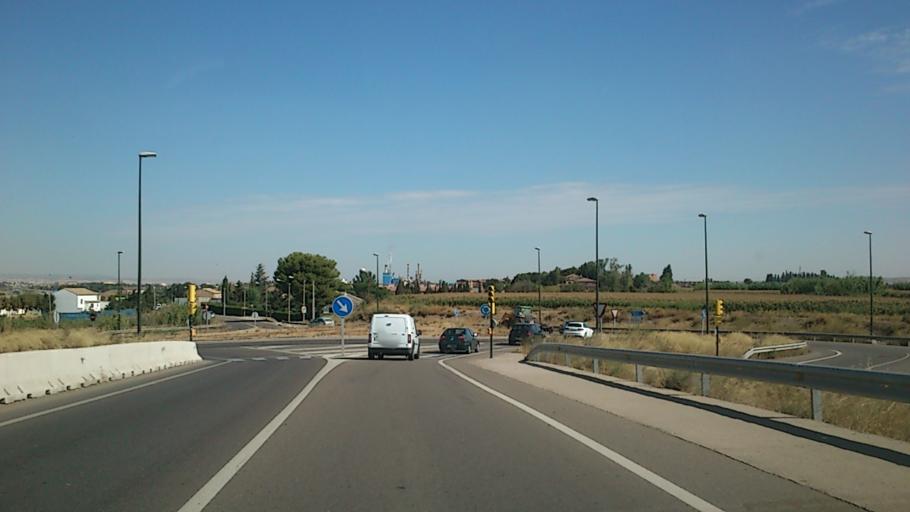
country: ES
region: Aragon
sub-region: Provincia de Zaragoza
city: Zaragoza
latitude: 41.6754
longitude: -0.8297
